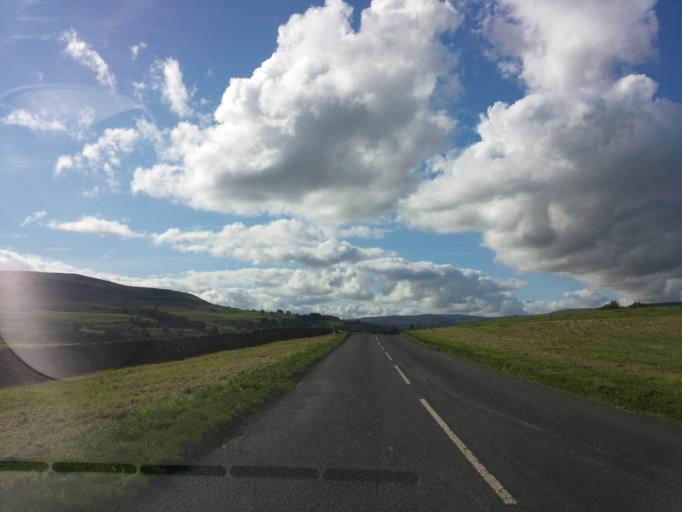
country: GB
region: England
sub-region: North Yorkshire
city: Leyburn
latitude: 54.2796
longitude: -1.8204
